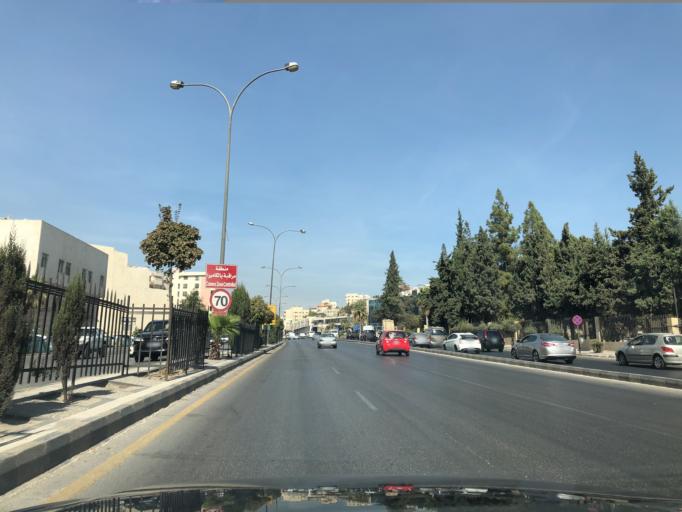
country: JO
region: Amman
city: Al Jubayhah
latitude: 32.0164
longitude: 35.8672
